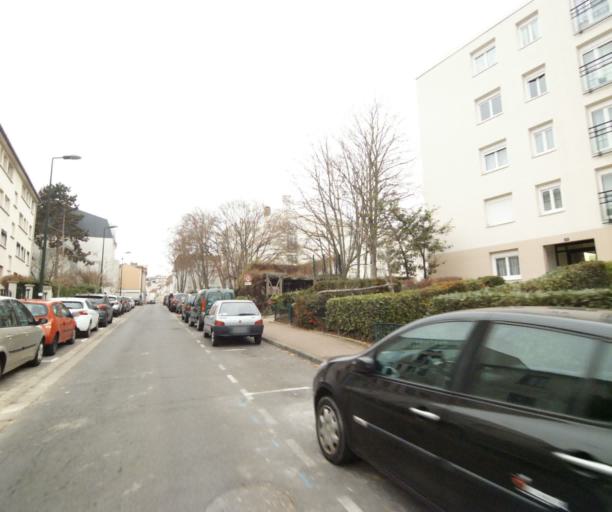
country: FR
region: Ile-de-France
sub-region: Departement des Hauts-de-Seine
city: Saint-Cloud
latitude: 48.8432
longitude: 2.1943
